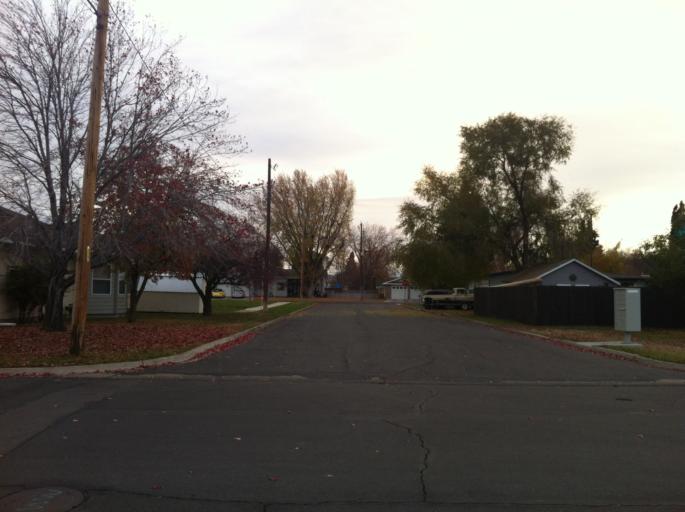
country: US
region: Oregon
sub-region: Baker County
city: Baker City
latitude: 44.7881
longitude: -117.8358
